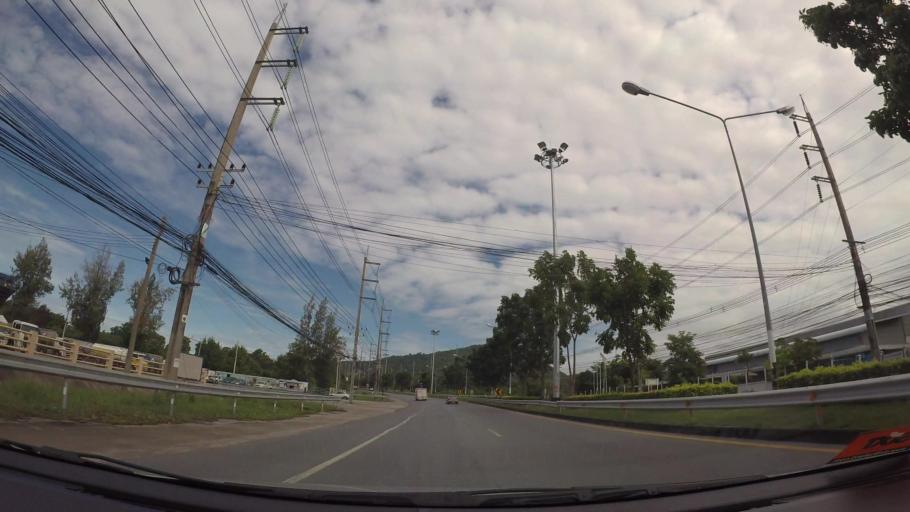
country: TH
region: Rayong
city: Ban Chang
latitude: 12.7480
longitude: 101.1089
